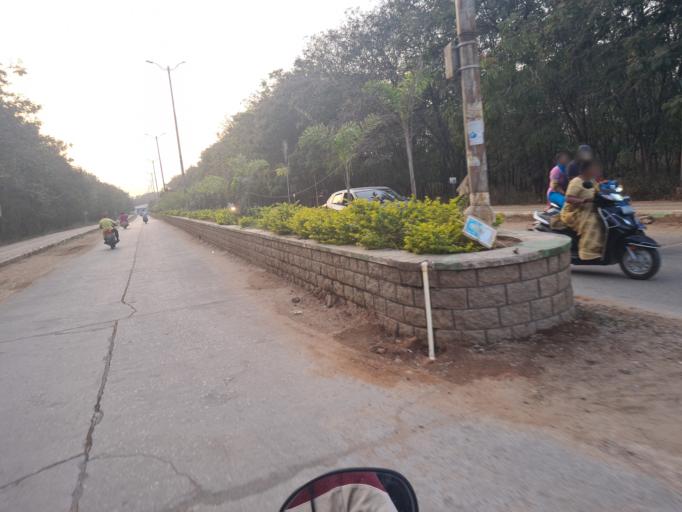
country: IN
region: Telangana
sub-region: Medak
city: Serilingampalle
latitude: 17.4780
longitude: 78.2946
